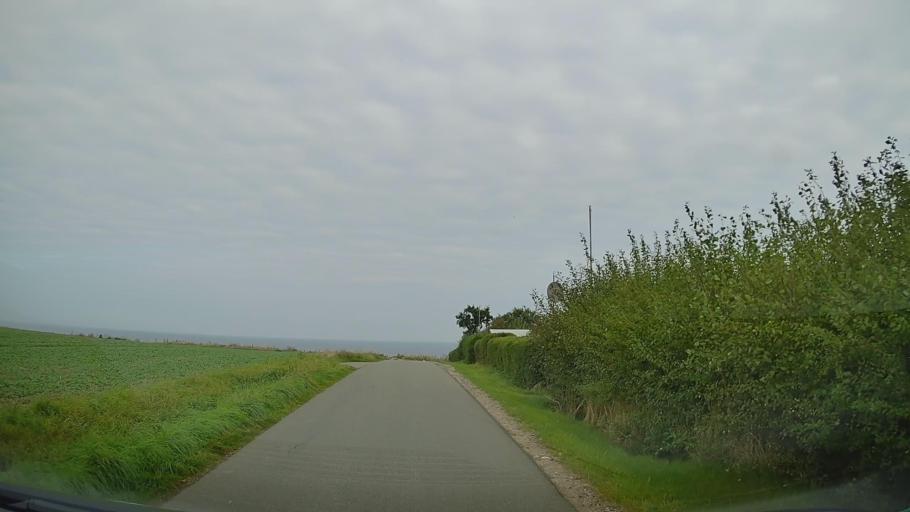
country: DE
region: Schleswig-Holstein
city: Hohenfelde
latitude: 54.3788
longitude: 10.5376
